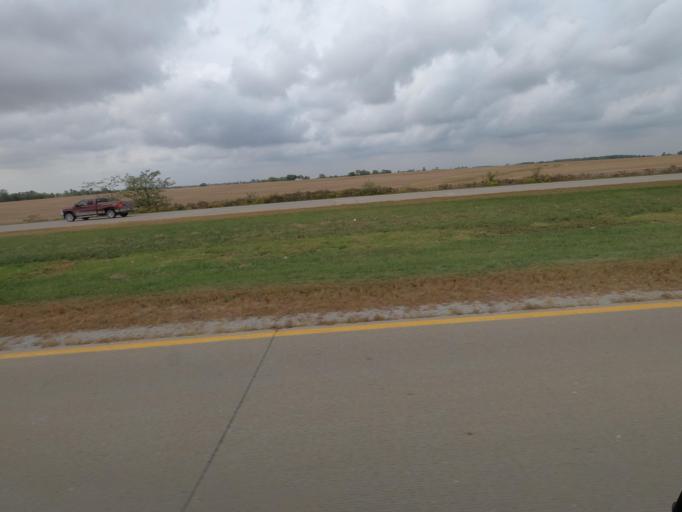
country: US
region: Iowa
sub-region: Wapello County
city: Ottumwa
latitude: 41.0019
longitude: -92.2645
